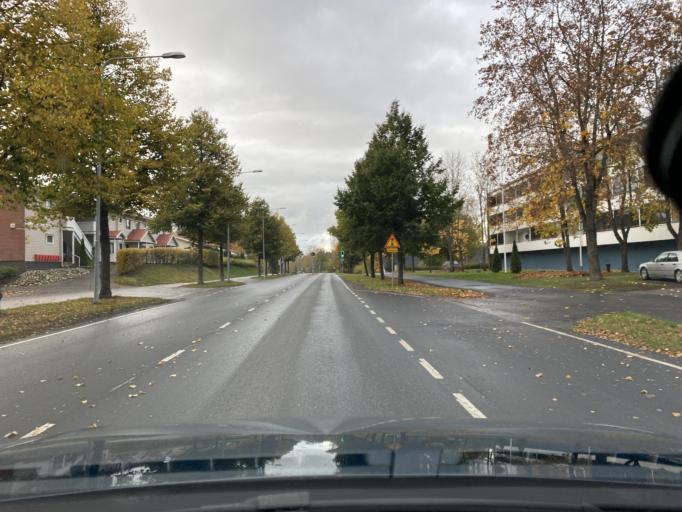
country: FI
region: Haeme
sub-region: Forssa
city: Forssa
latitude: 60.8203
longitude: 23.6081
